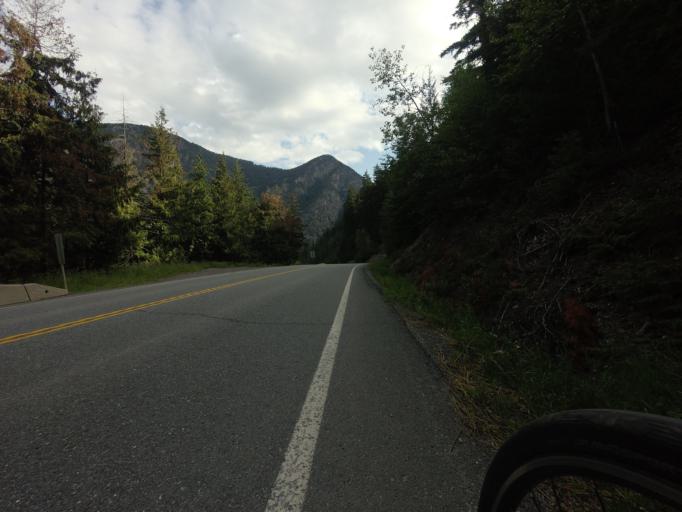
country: CA
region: British Columbia
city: Lillooet
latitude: 50.6317
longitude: -122.0895
